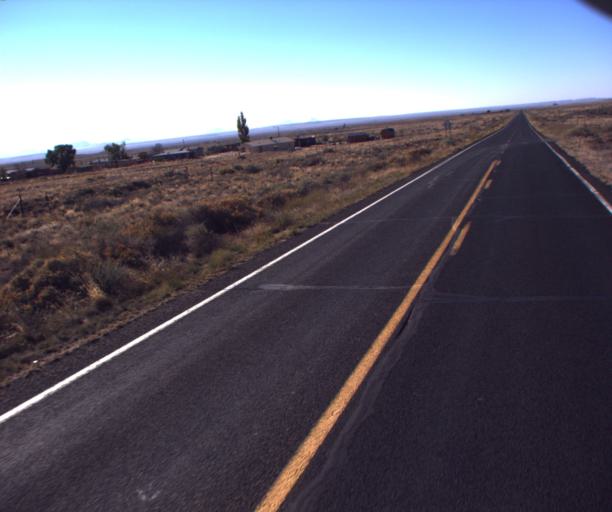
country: US
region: Arizona
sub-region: Navajo County
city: First Mesa
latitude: 35.7871
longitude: -110.4988
